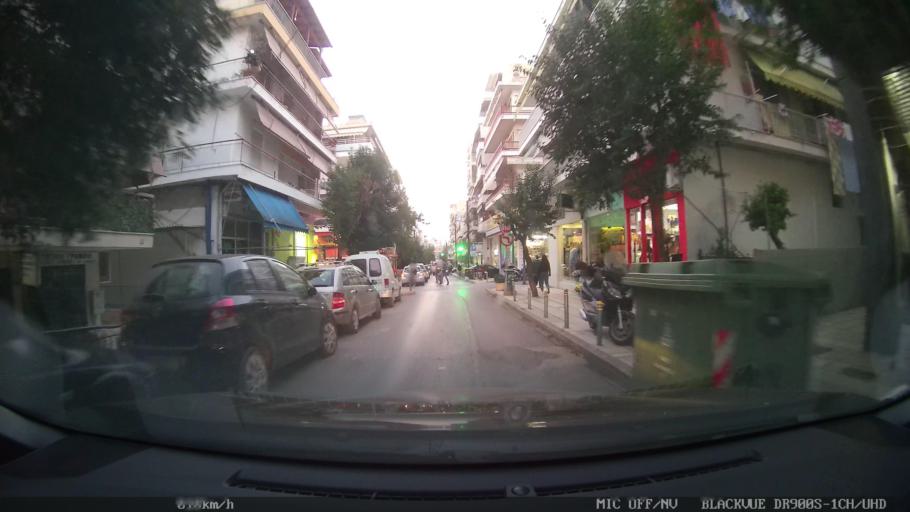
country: GR
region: Central Macedonia
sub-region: Nomos Thessalonikis
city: Kalamaria
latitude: 40.5792
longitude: 22.9499
